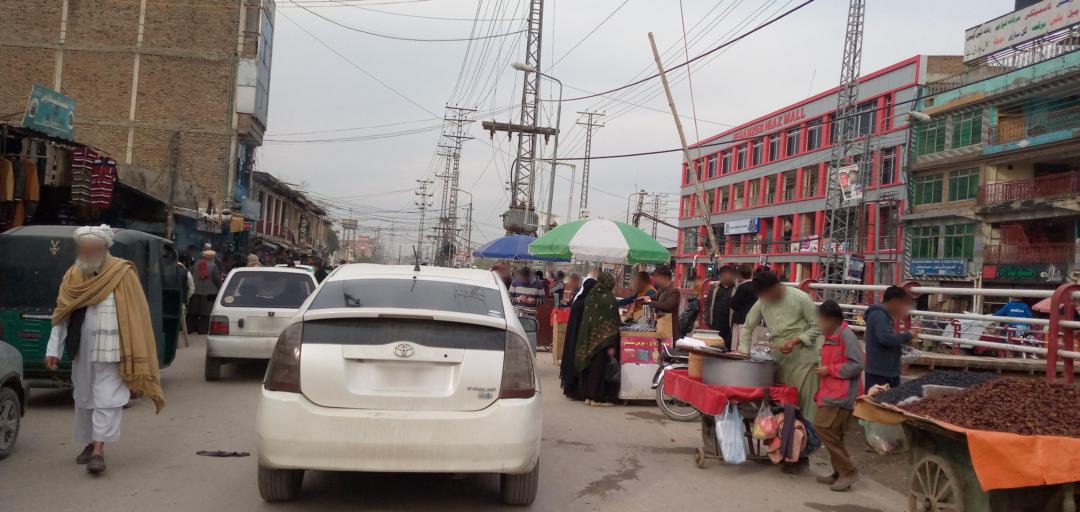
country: PK
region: Khyber Pakhtunkhwa
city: Peshawar
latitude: 33.9965
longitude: 71.4698
